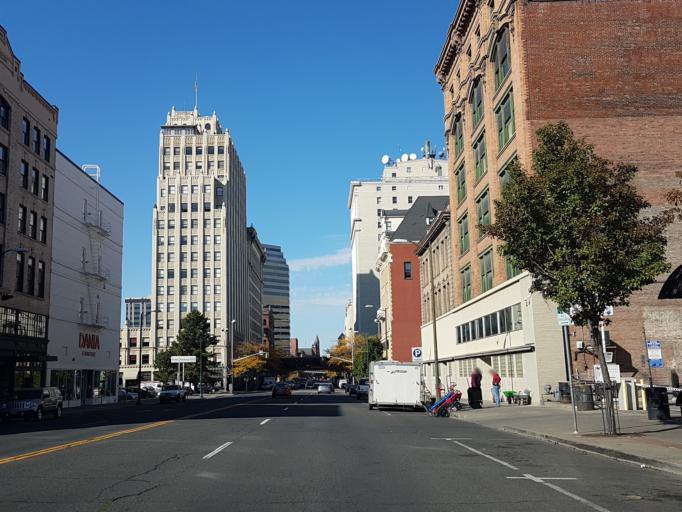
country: US
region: Washington
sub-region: Spokane County
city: Spokane
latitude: 47.6580
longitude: -117.4162
